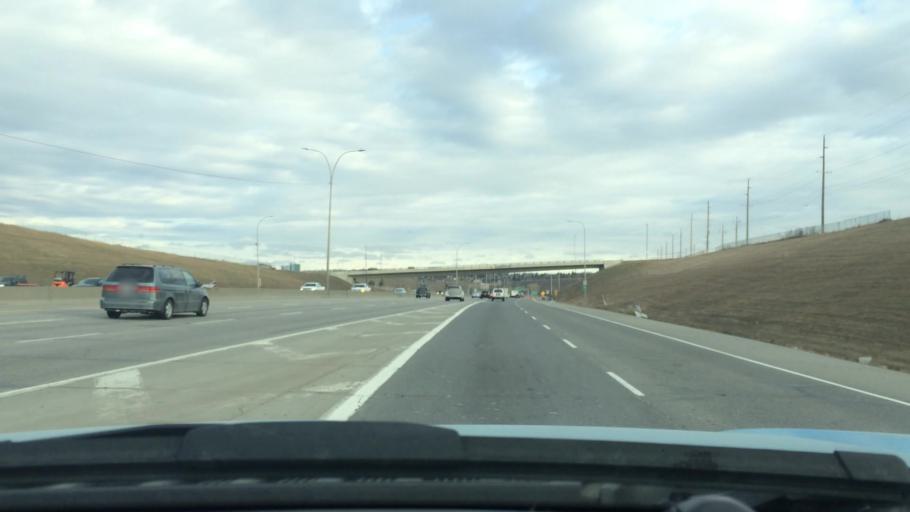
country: CA
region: Alberta
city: Calgary
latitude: 51.0210
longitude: -114.0018
